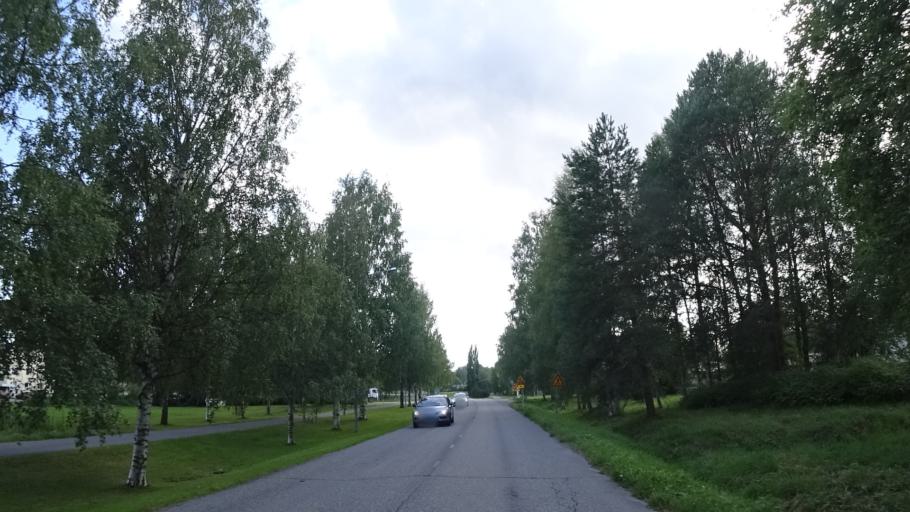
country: FI
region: North Karelia
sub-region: Pielisen Karjala
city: Lieksa
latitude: 63.3304
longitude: 30.0266
